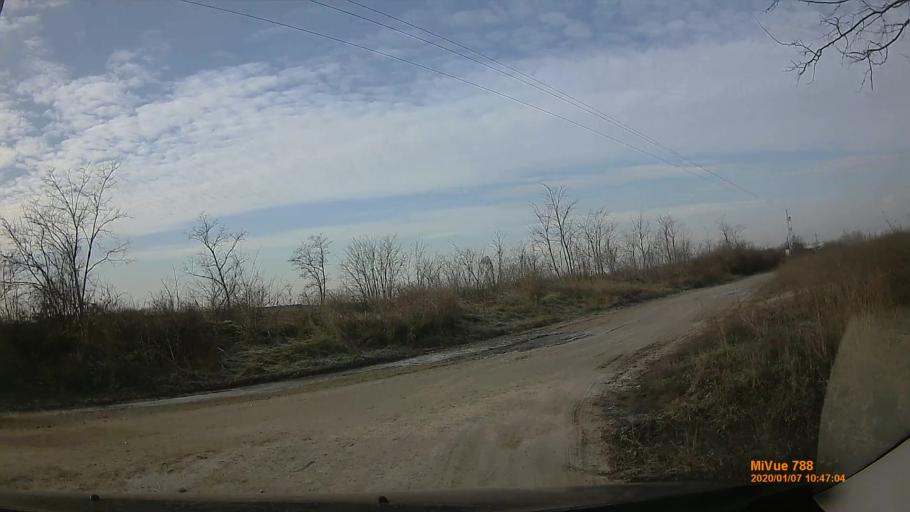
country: HU
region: Gyor-Moson-Sopron
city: Rajka
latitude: 47.9126
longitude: 17.1851
